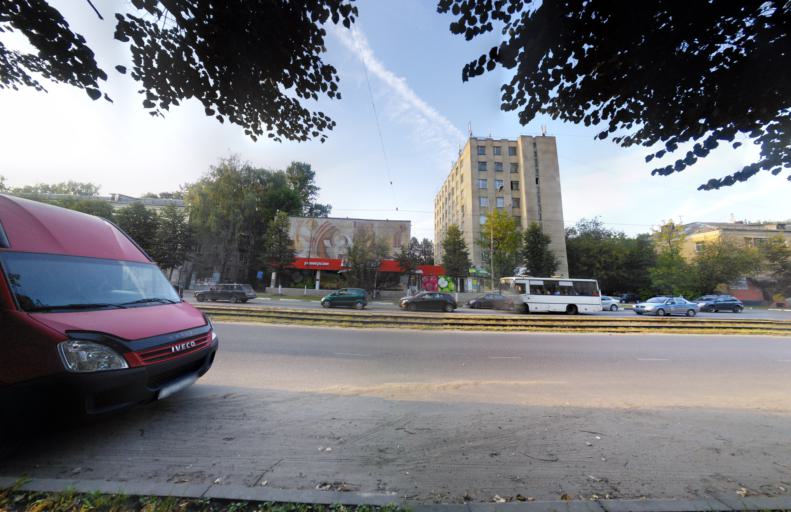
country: RU
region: Jaroslavl
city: Yaroslavl
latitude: 57.6379
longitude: 39.8258
